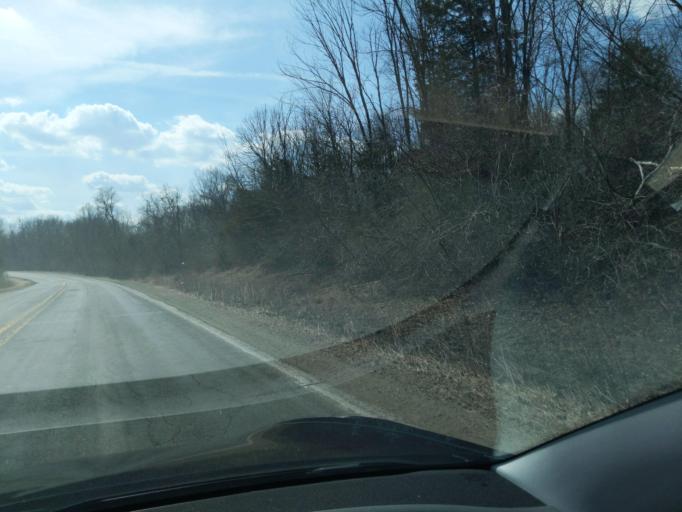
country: US
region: Michigan
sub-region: Washtenaw County
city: Chelsea
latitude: 42.4093
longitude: -84.0446
